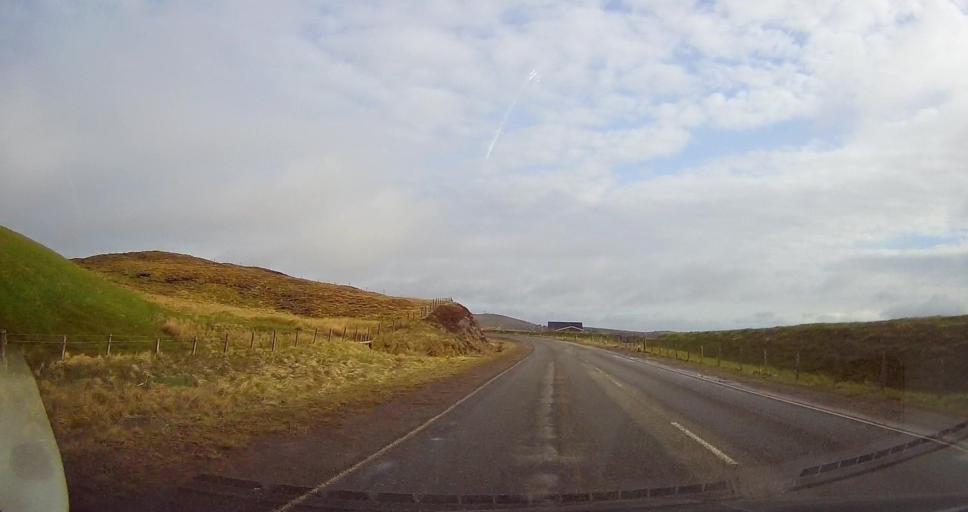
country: GB
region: Scotland
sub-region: Shetland Islands
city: Lerwick
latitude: 60.1181
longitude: -1.2161
